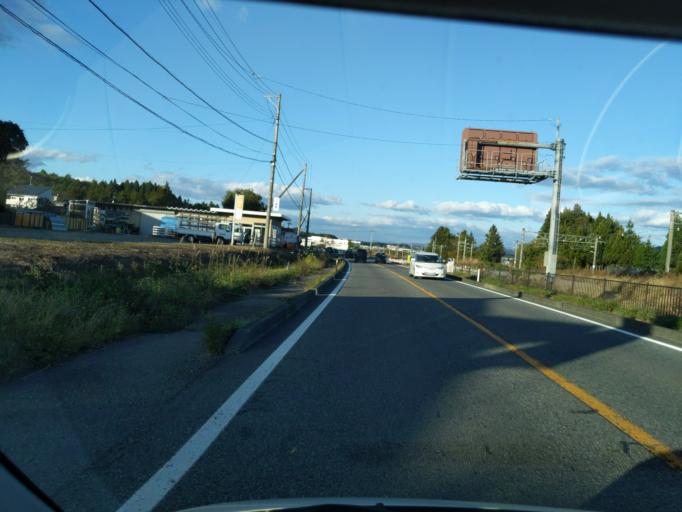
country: JP
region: Iwate
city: Kitakami
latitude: 39.2402
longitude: 141.0980
